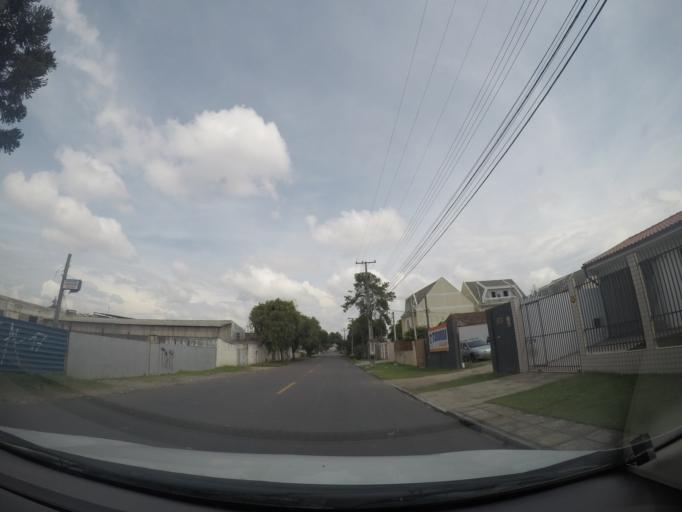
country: BR
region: Parana
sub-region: Curitiba
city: Curitiba
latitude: -25.4757
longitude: -49.2613
